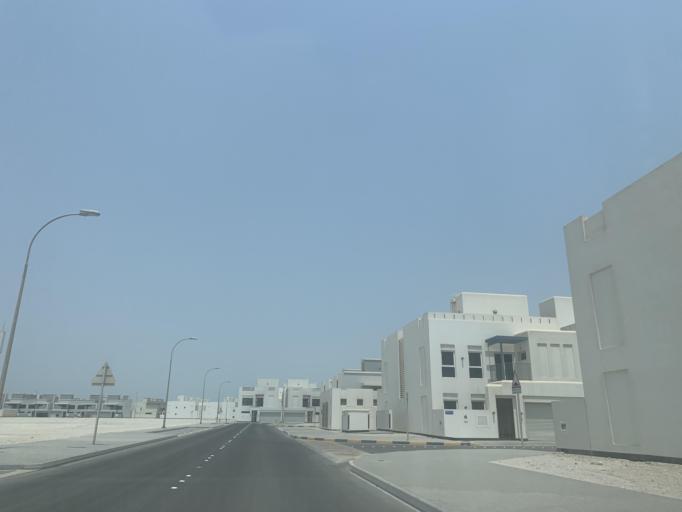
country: BH
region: Muharraq
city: Al Muharraq
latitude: 26.3128
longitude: 50.6214
